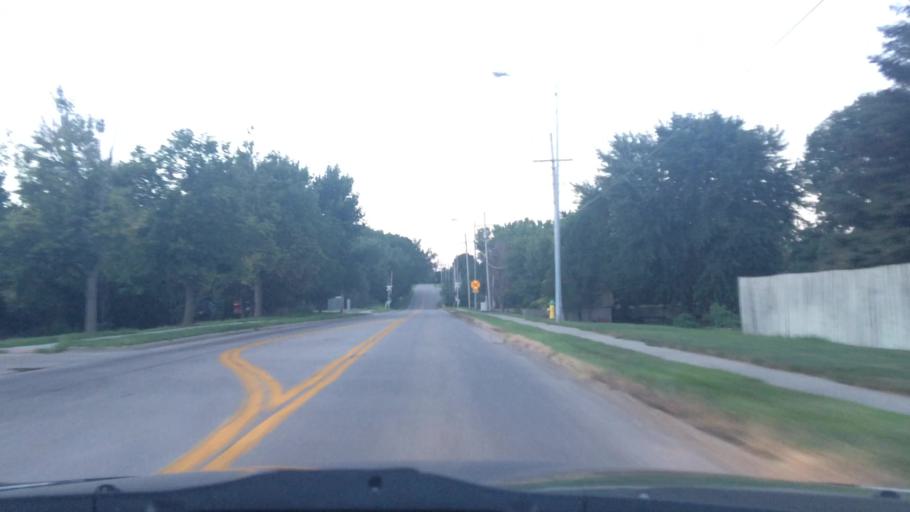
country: US
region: Nebraska
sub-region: Douglas County
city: Ralston
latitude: 41.1967
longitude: -96.0524
